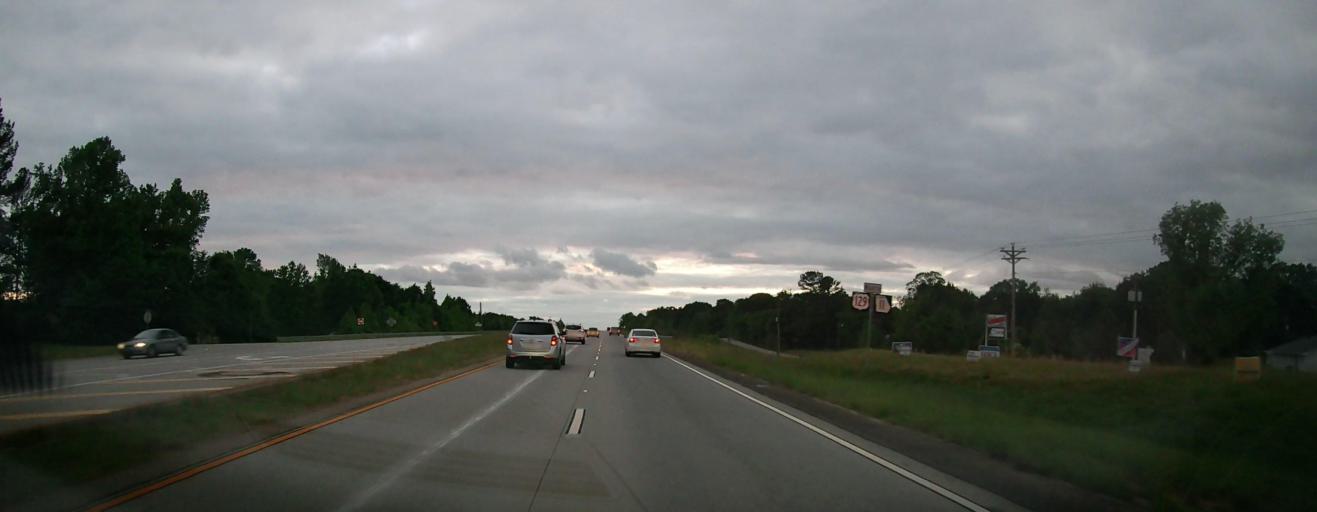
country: US
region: Georgia
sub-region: Jackson County
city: Arcade
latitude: 34.0739
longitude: -83.5583
